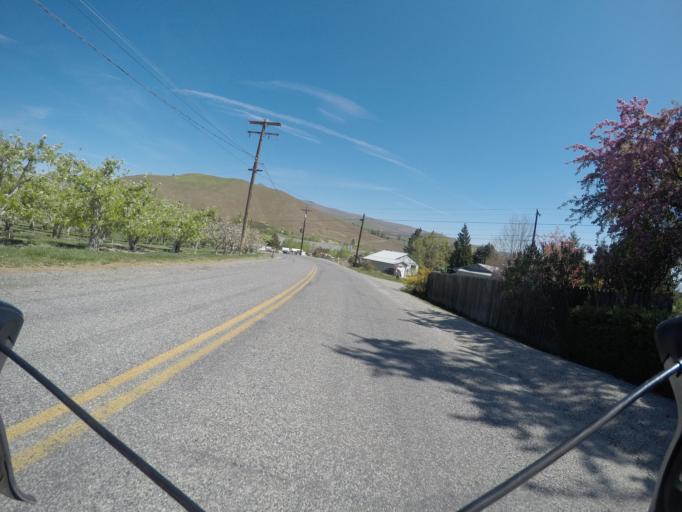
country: US
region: Washington
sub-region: Chelan County
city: Cashmere
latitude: 47.4831
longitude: -120.4186
